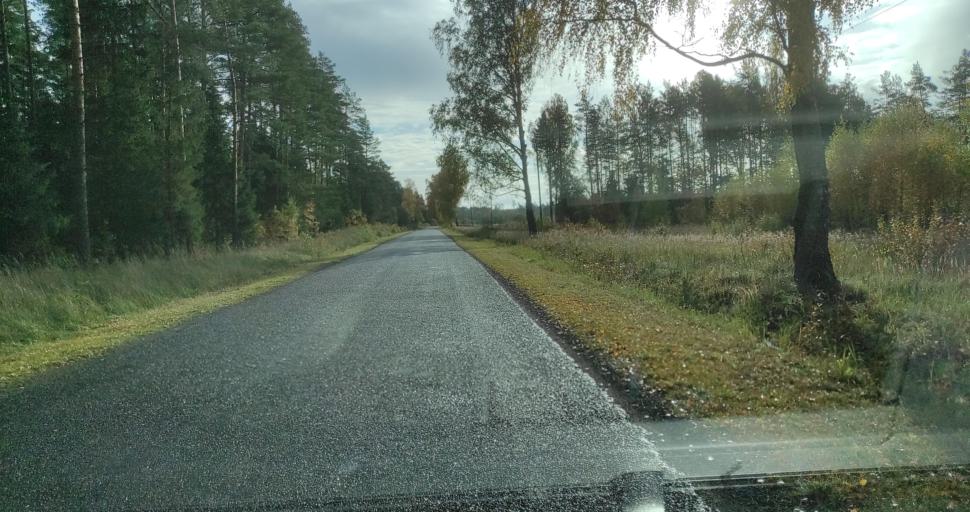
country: LV
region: Skrunda
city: Skrunda
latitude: 56.6844
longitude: 22.0615
